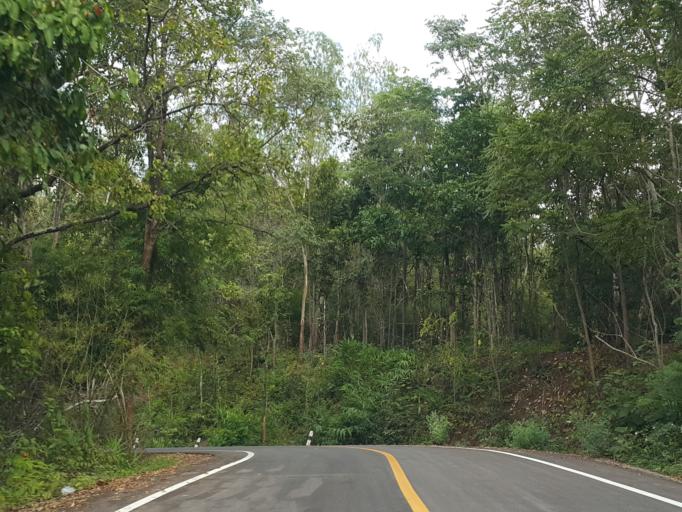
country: TH
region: Lampang
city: Chae Hom
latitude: 18.6528
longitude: 99.5245
